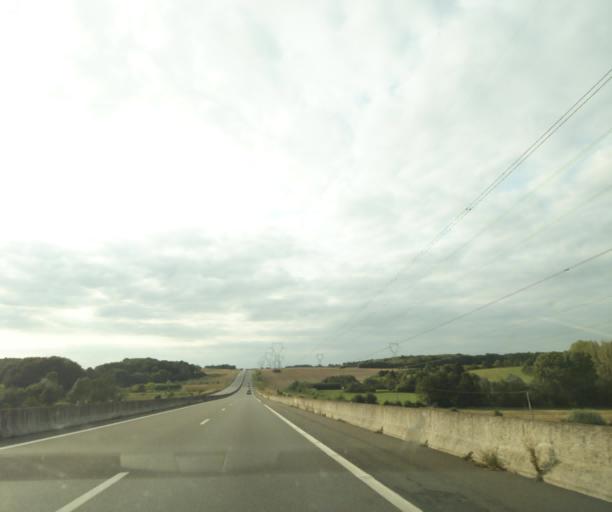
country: FR
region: Centre
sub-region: Departement d'Indre-et-Loire
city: Cerelles
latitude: 47.4850
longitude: 0.6774
